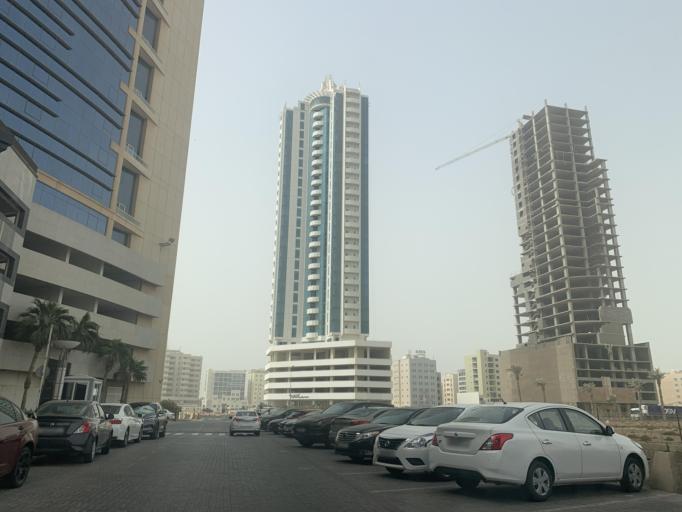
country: BH
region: Manama
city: Jidd Hafs
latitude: 26.2302
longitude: 50.5585
